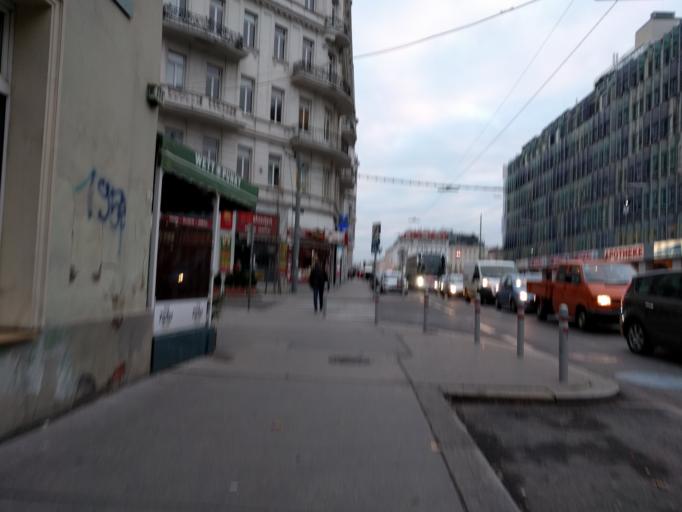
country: AT
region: Vienna
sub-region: Wien Stadt
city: Vienna
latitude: 48.2265
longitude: 16.3634
